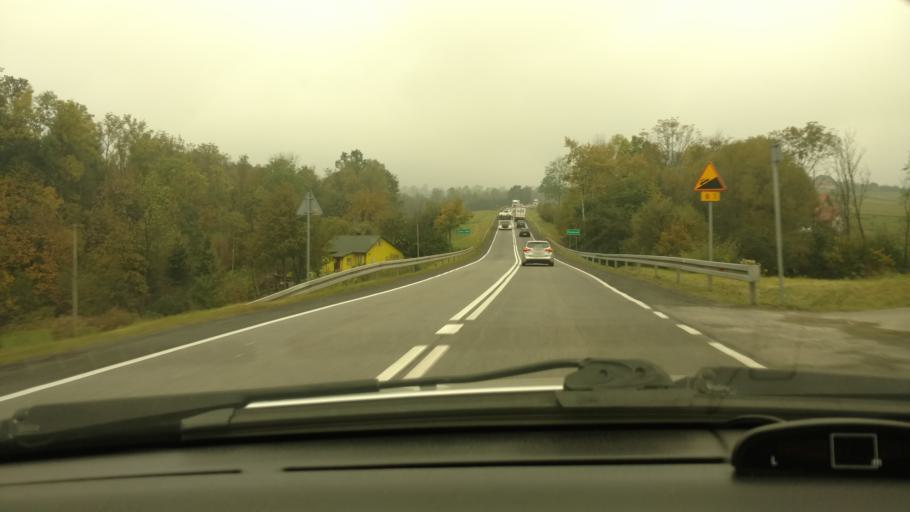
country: PL
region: Lesser Poland Voivodeship
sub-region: Powiat nowosadecki
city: Grybow
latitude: 49.6188
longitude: 20.8938
